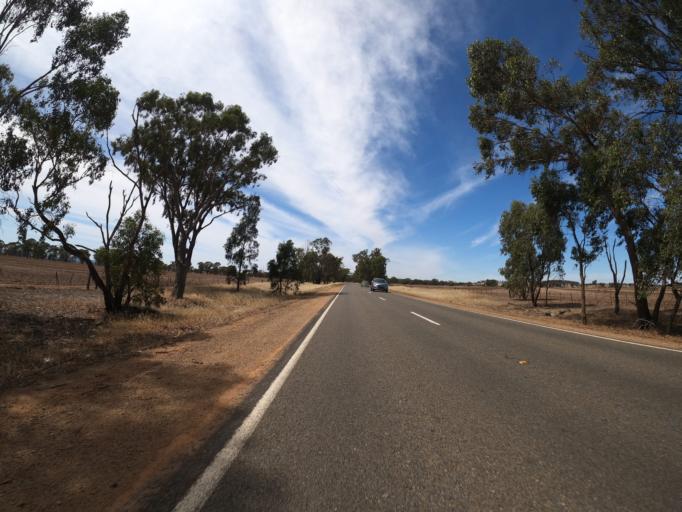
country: AU
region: Victoria
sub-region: Benalla
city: Benalla
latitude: -36.3013
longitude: 145.9541
